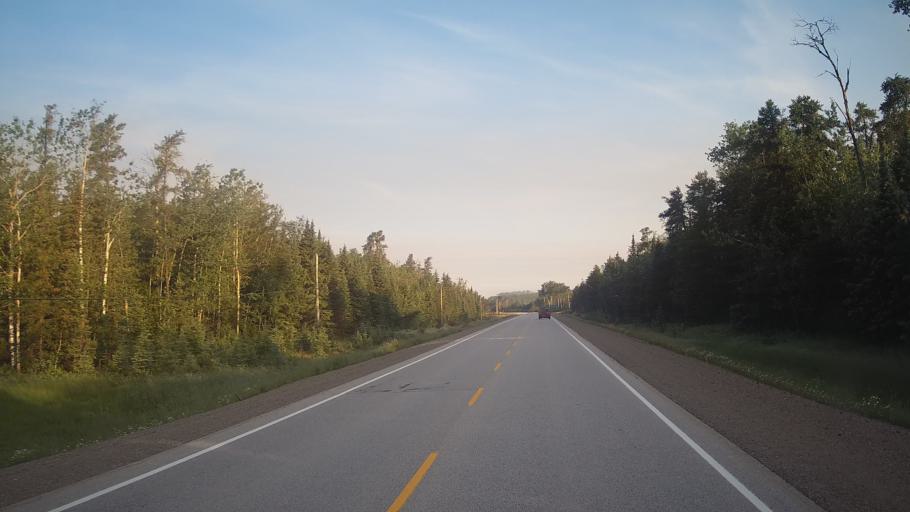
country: CA
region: Ontario
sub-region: Rainy River District
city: Atikokan
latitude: 49.2489
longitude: -91.1011
